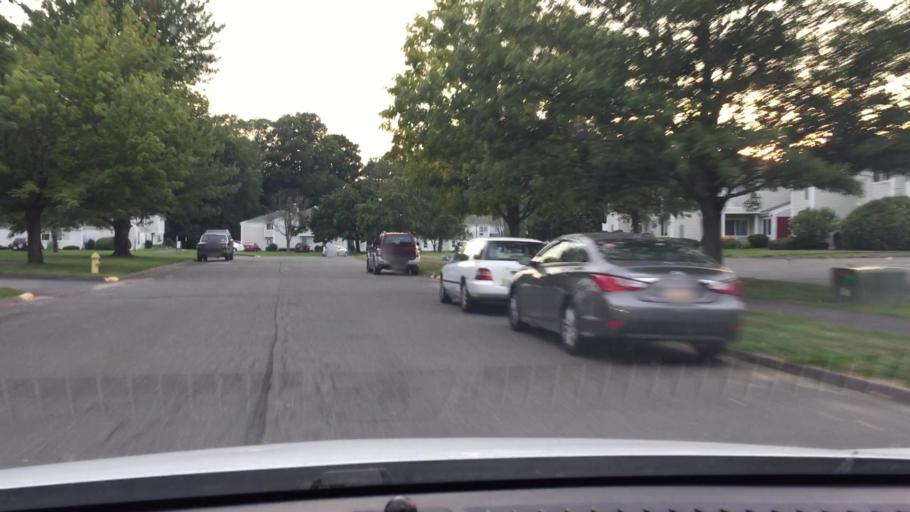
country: US
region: Massachusetts
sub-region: Hampden County
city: Agawam
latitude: 42.0610
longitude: -72.6905
